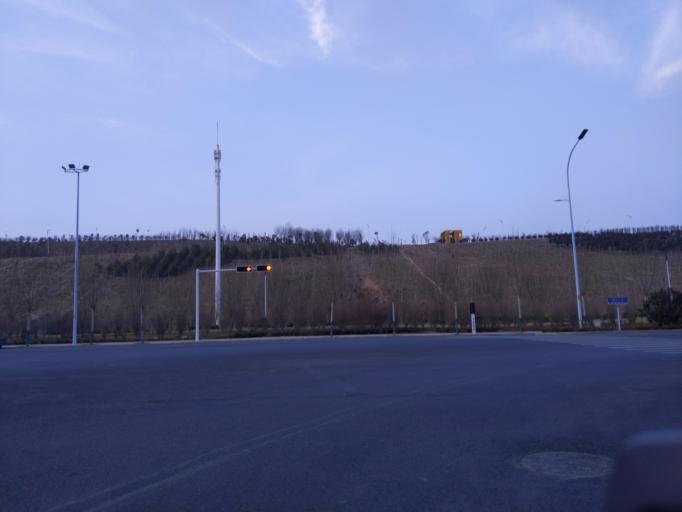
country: CN
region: Henan Sheng
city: Puyang
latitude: 35.8176
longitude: 115.0119
